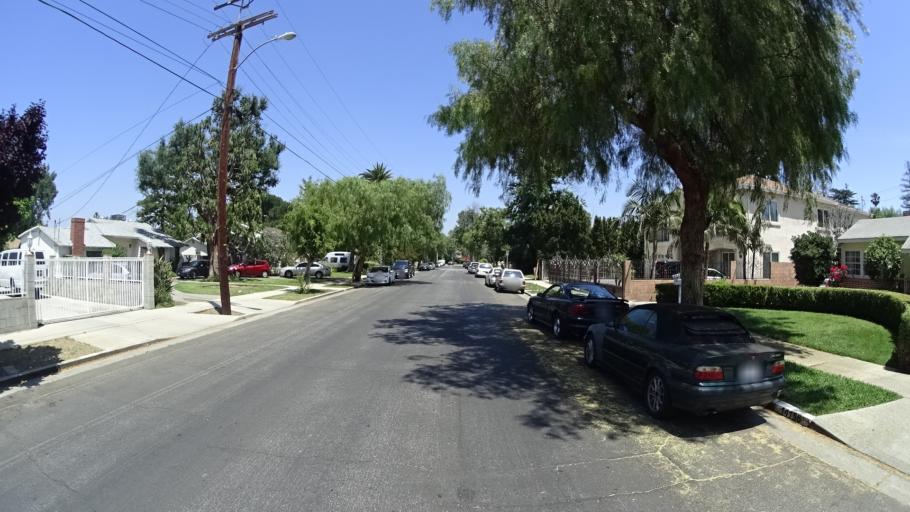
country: US
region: California
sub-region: Los Angeles County
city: Van Nuys
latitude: 34.1896
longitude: -118.4420
